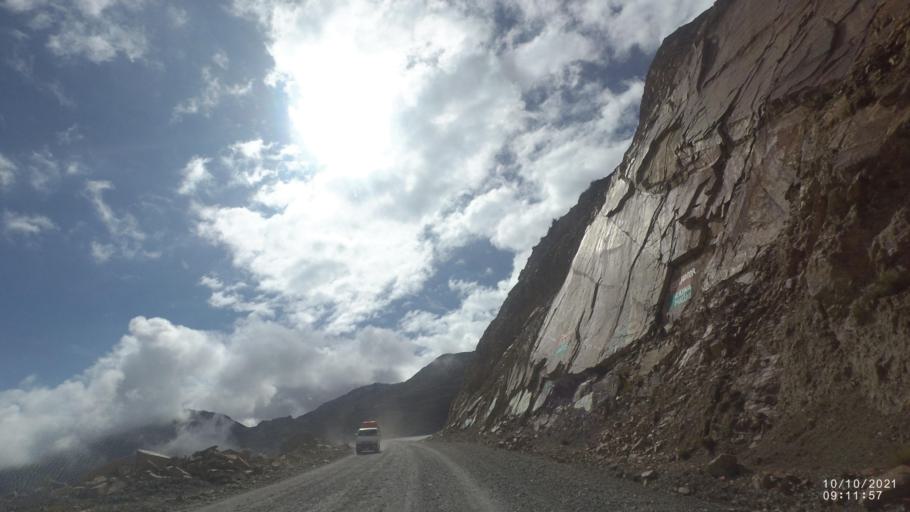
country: BO
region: La Paz
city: Quime
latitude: -17.0281
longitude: -67.2886
